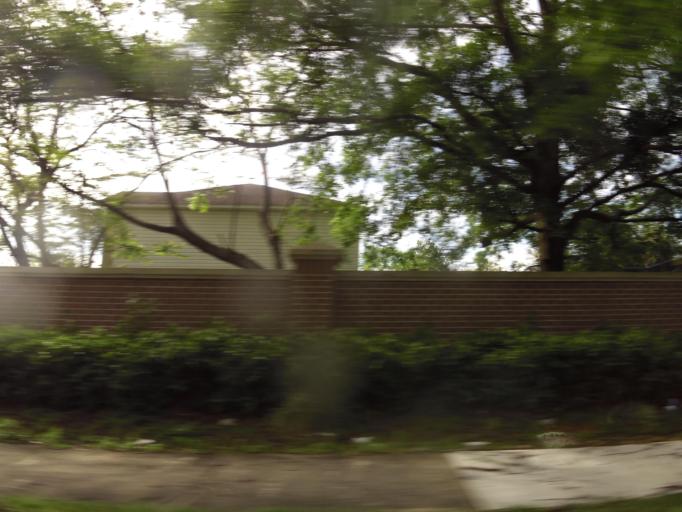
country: US
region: Florida
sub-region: Clay County
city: Bellair-Meadowbrook Terrace
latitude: 30.2608
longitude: -81.7818
